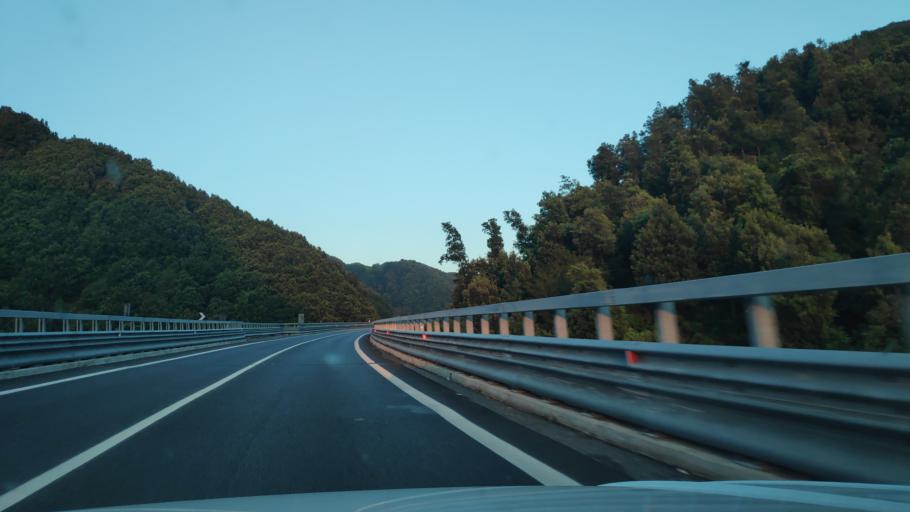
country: IT
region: Calabria
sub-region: Provincia di Reggio Calabria
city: Giffone
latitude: 38.4135
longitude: 16.1362
